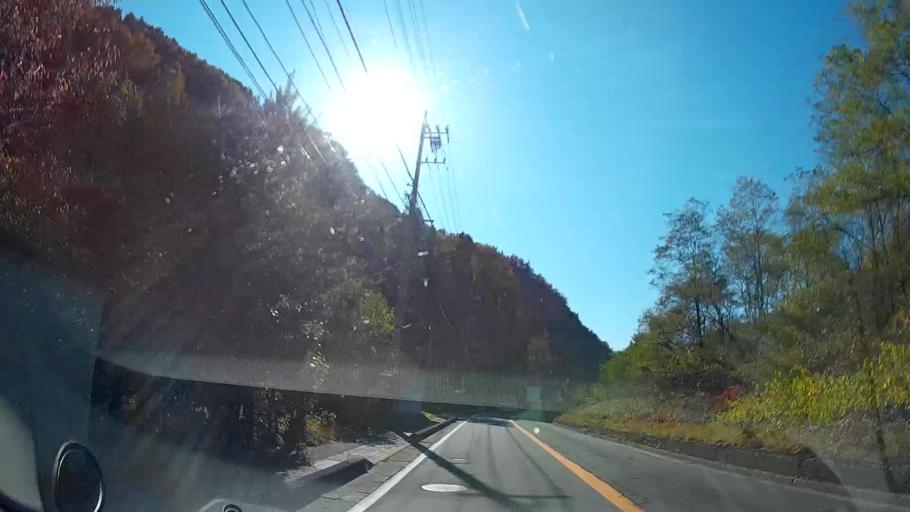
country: JP
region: Nagano
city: Toyoshina
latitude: 36.1881
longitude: 137.8160
